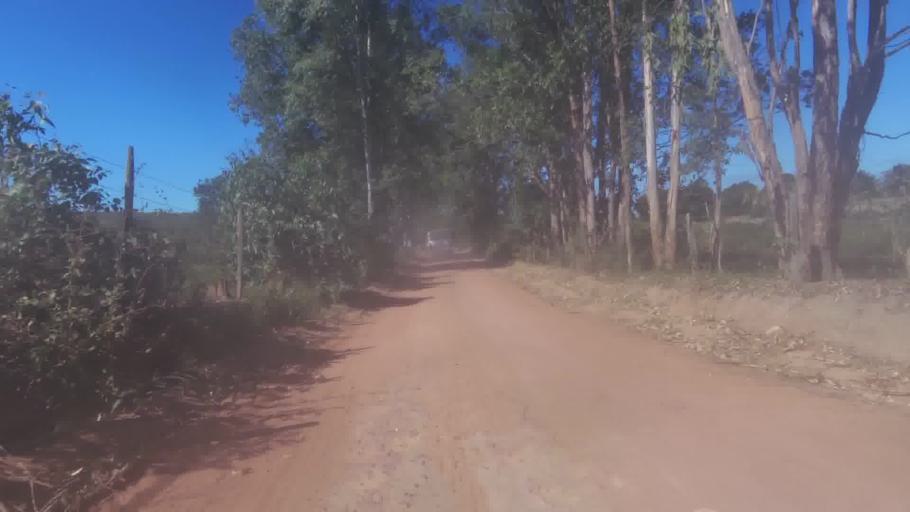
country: BR
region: Espirito Santo
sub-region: Marataizes
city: Marataizes
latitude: -21.1230
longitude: -40.9767
